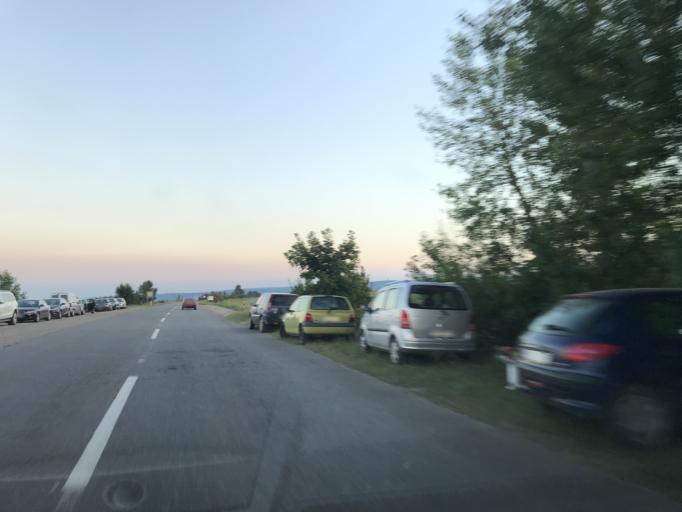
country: RS
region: Central Serbia
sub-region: Borski Okrug
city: Negotin
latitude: 44.2621
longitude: 22.5176
